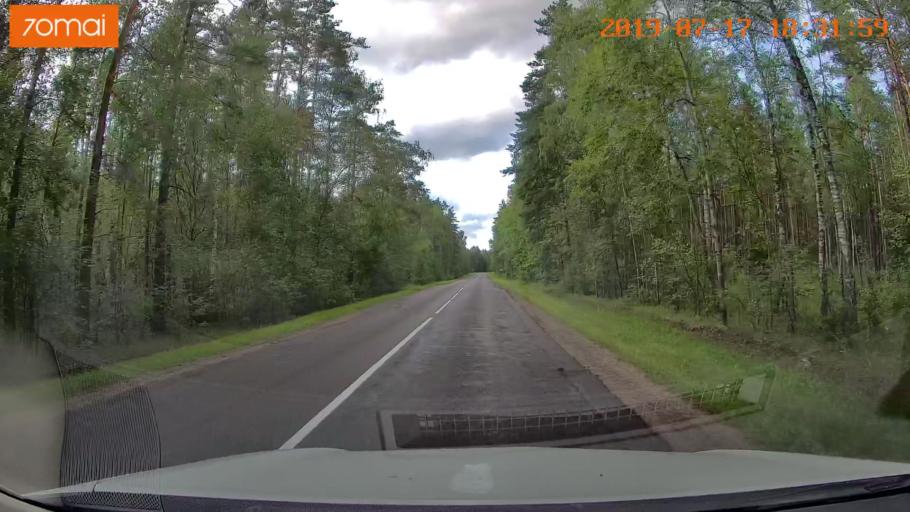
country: BY
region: Mogilev
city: Asipovichy
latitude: 53.2653
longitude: 28.6779
